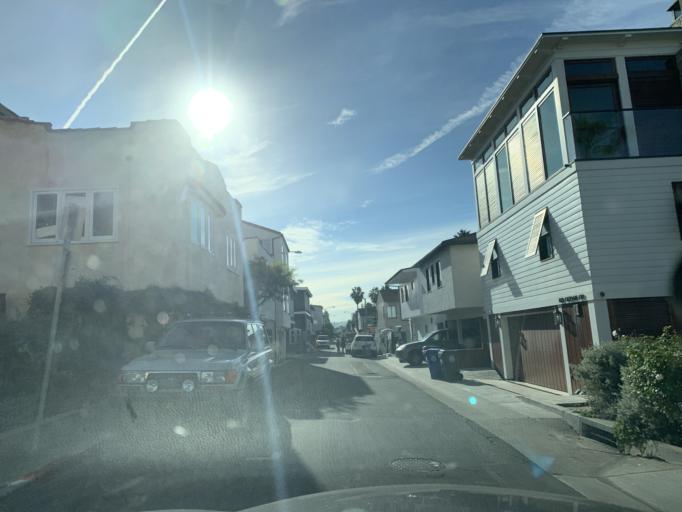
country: US
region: California
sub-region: Los Angeles County
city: Manhattan Beach
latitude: 33.8814
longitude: -118.4097
